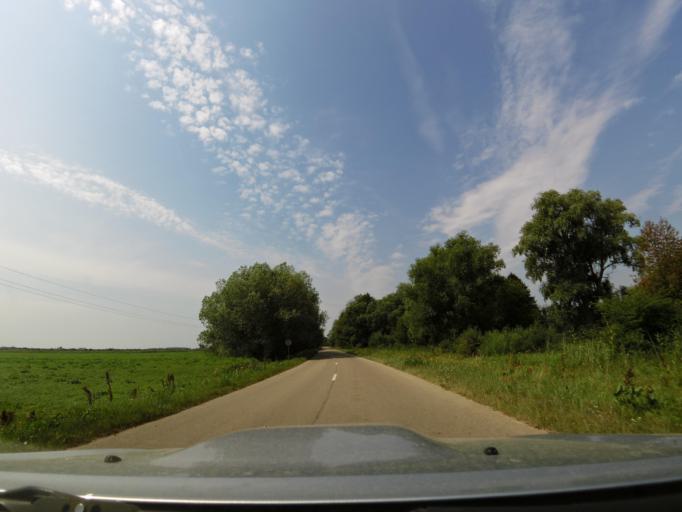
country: LT
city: Rusne
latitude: 55.3449
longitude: 21.3125
